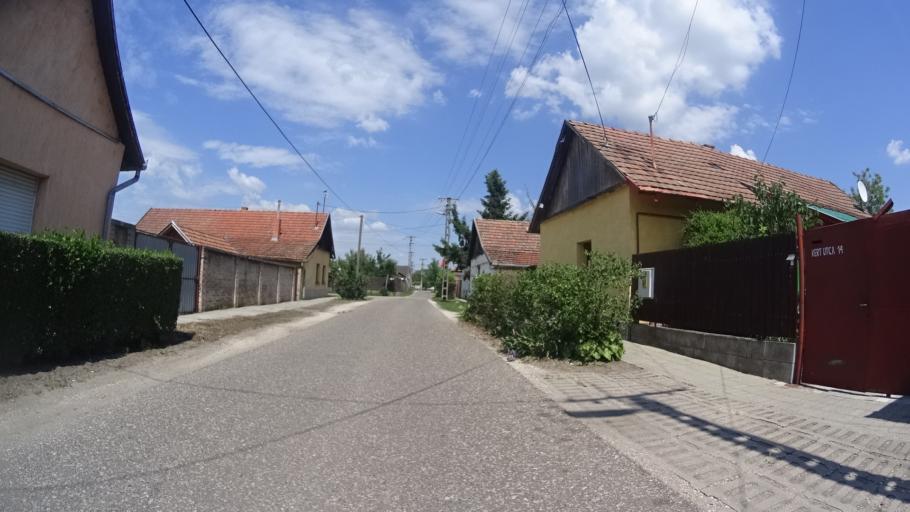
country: HU
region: Bacs-Kiskun
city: Tiszakecske
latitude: 46.9384
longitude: 20.0871
